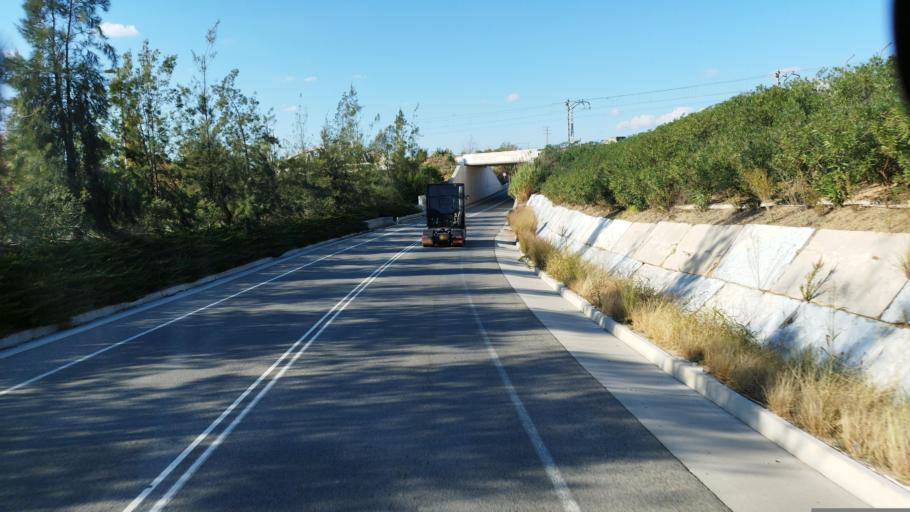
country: ES
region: Catalonia
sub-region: Provincia de Tarragona
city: Vila-seca
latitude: 41.1023
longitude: 1.1611
